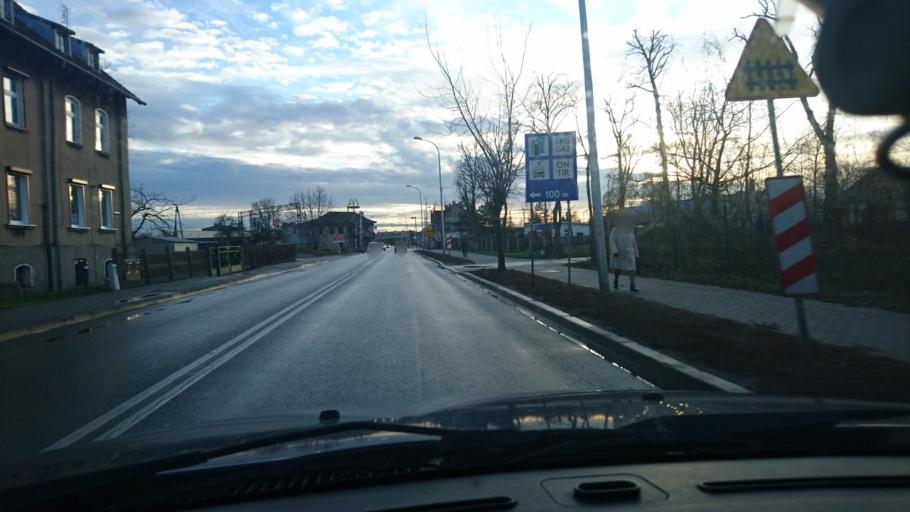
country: PL
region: Greater Poland Voivodeship
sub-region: Powiat kepinski
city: Kepno
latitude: 51.2912
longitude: 17.9945
